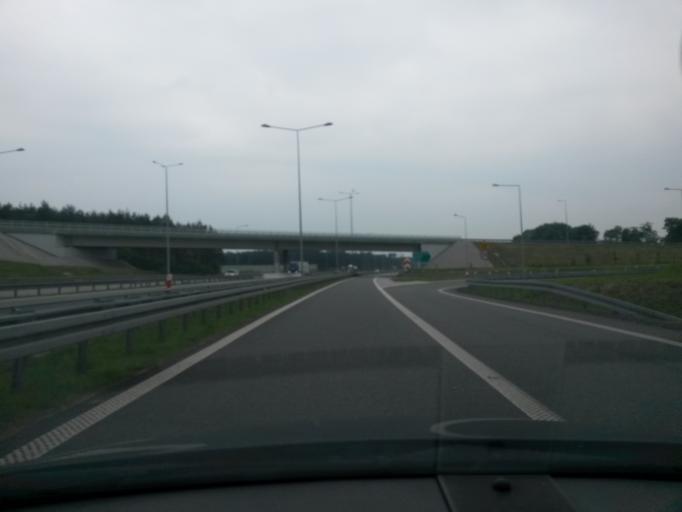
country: PL
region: Lodz Voivodeship
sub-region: Powiat tomaszowski
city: Tomaszow Mazowiecki
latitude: 51.5257
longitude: 19.9406
